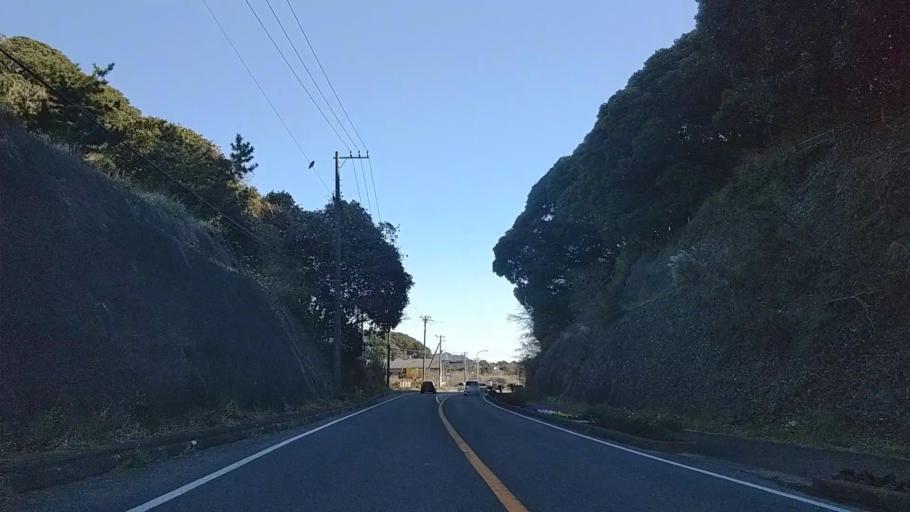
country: JP
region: Chiba
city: Kawaguchi
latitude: 35.1237
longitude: 140.1421
